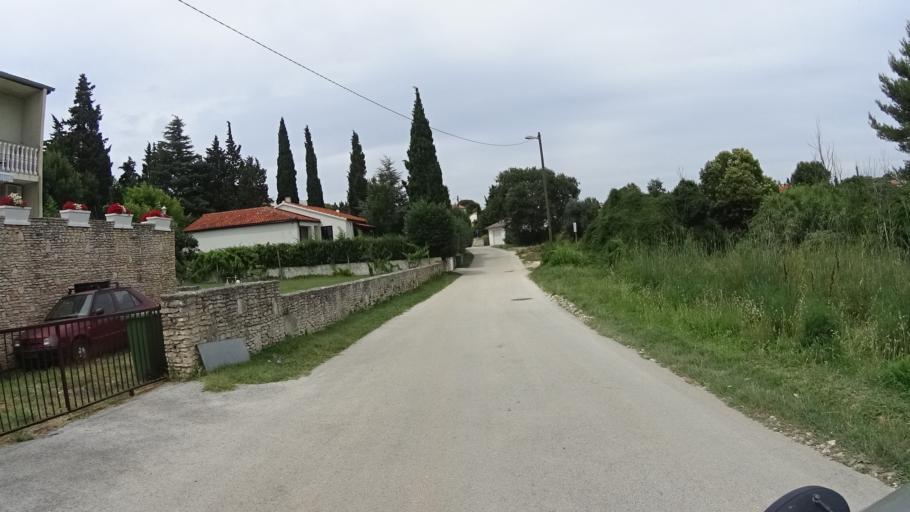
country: HR
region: Istarska
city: Medulin
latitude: 44.8008
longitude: 13.9145
